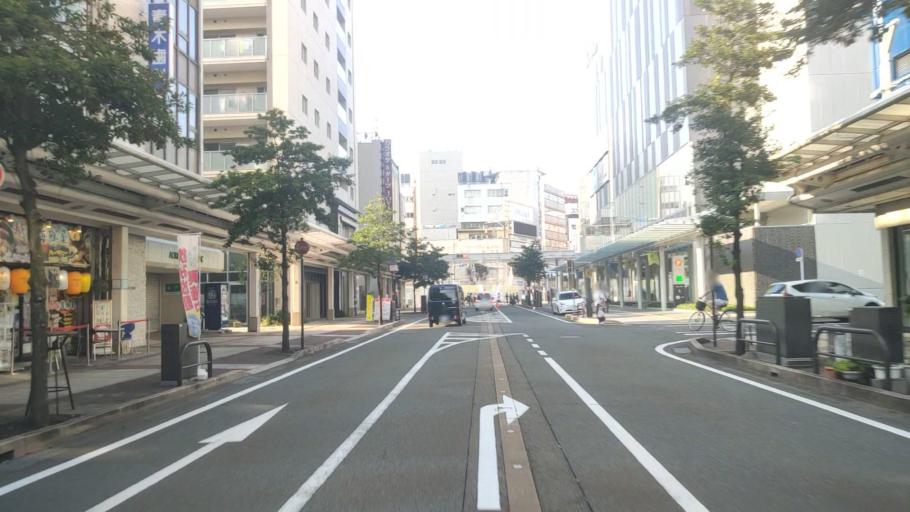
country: JP
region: Fukui
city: Fukui-shi
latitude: 36.0609
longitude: 136.2214
